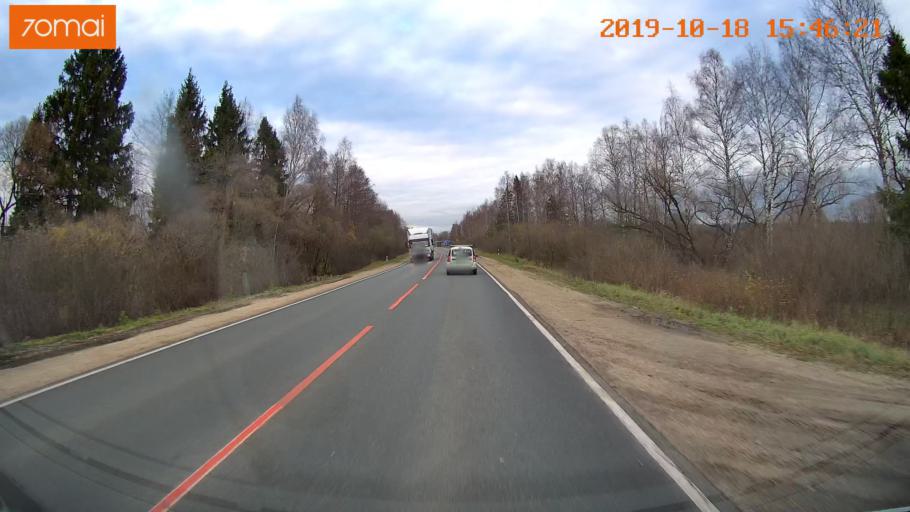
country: RU
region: Vladimir
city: Golovino
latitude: 56.0062
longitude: 40.5694
